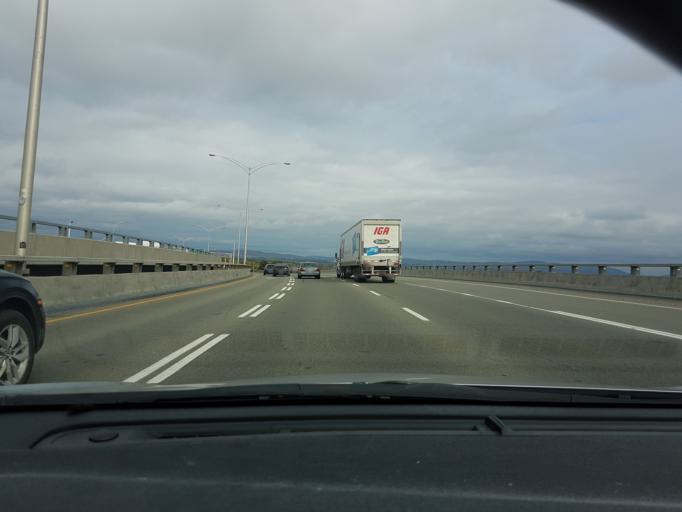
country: CA
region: Quebec
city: L'Ancienne-Lorette
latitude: 46.8003
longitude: -71.2859
